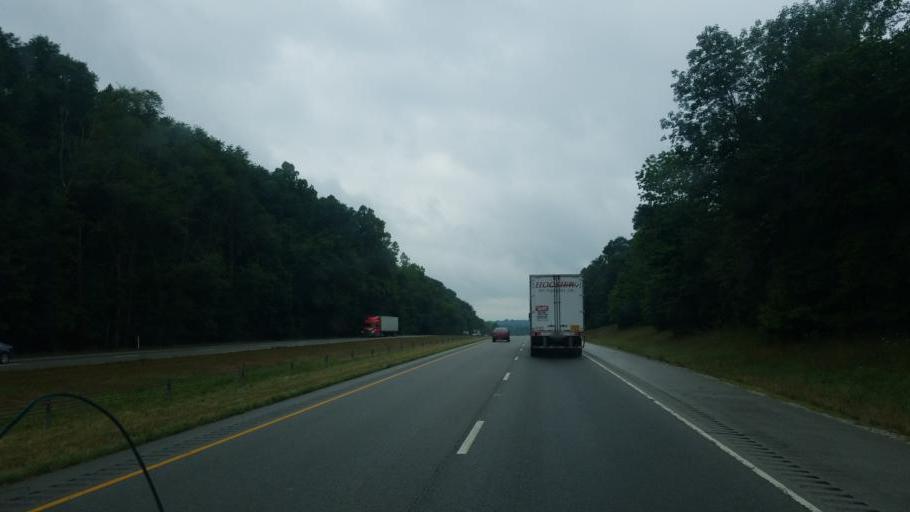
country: US
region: Indiana
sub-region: Putnam County
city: Cloverdale
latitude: 39.5109
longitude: -86.9328
